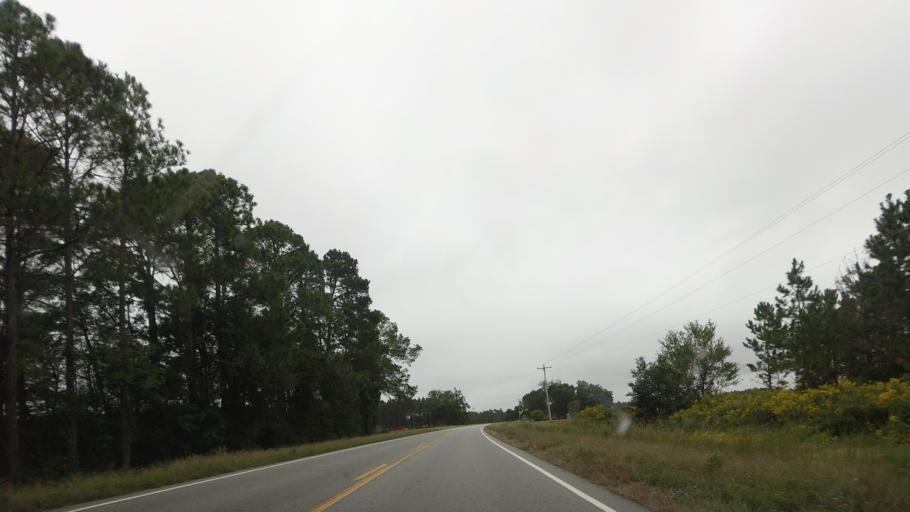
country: US
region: Georgia
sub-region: Berrien County
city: Nashville
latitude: 31.2854
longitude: -83.2390
